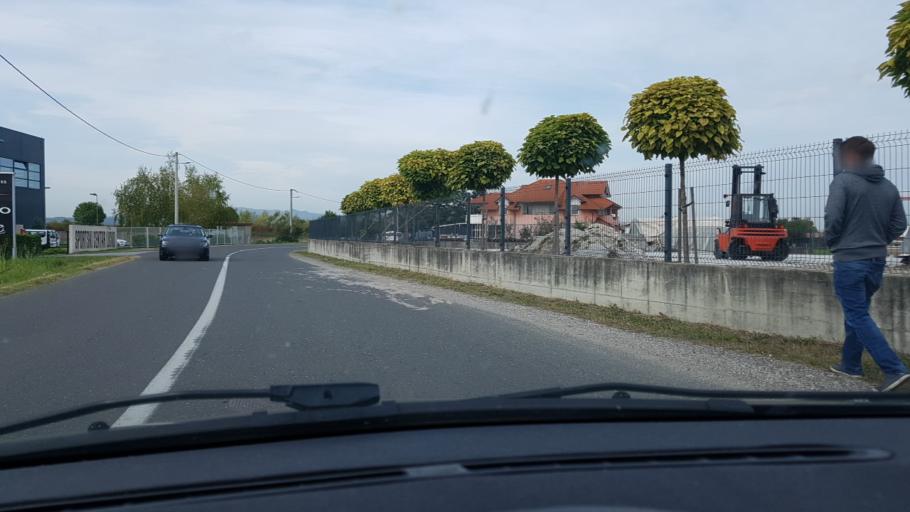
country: HR
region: Grad Zagreb
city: Lucko
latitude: 45.7634
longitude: 15.8693
